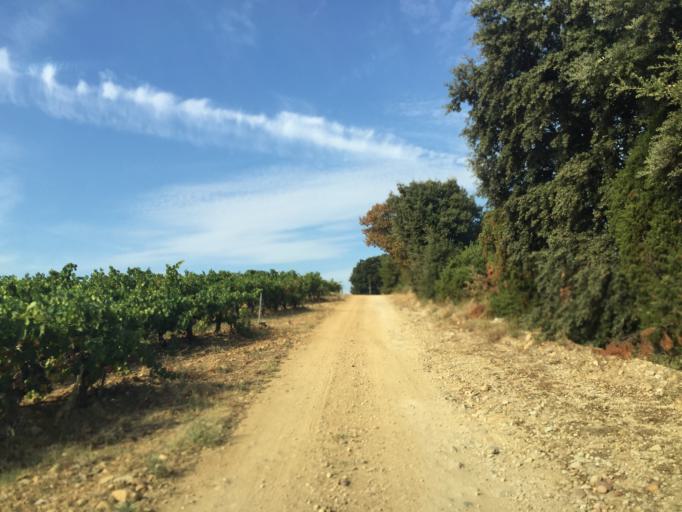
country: FR
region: Provence-Alpes-Cote d'Azur
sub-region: Departement du Vaucluse
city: Courthezon
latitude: 44.0779
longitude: 4.8558
